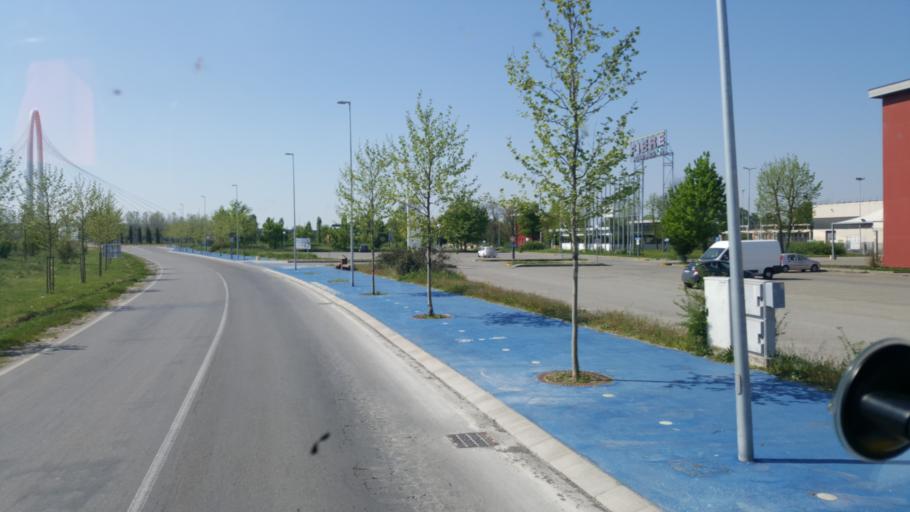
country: IT
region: Emilia-Romagna
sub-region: Provincia di Reggio Emilia
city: Reggio nell'Emilia
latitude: 44.7302
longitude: 10.6445
